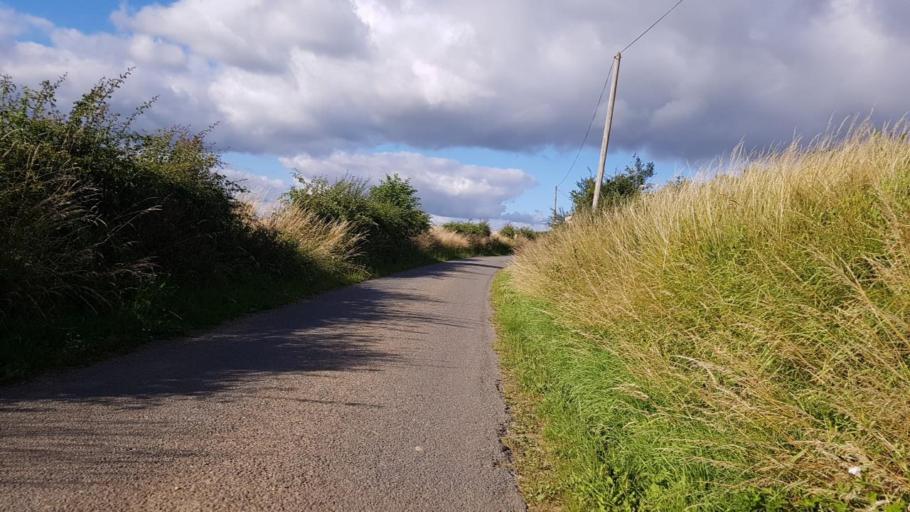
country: FR
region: Picardie
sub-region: Departement de l'Aisne
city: Hirson
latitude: 49.9293
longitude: 4.0444
